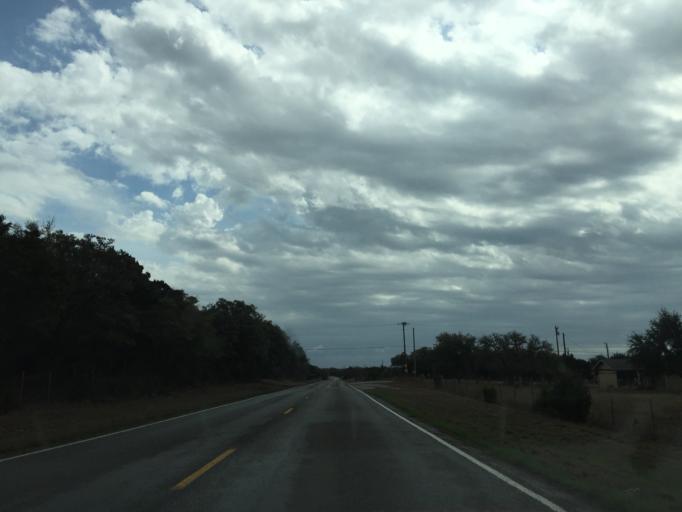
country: US
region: Texas
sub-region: Burnet County
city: Bertram
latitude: 30.6534
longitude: -97.9904
